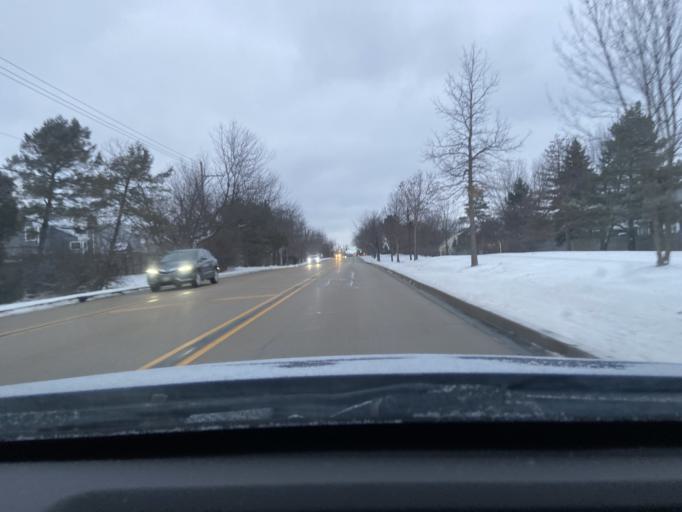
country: US
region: Illinois
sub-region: Lake County
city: Grayslake
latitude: 42.3483
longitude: -88.0241
